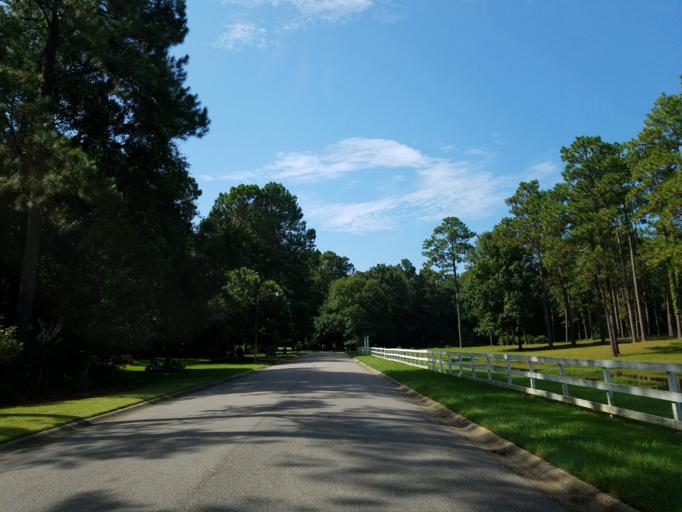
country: US
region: Mississippi
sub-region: Lamar County
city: West Hattiesburg
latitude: 31.3155
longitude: -89.3453
